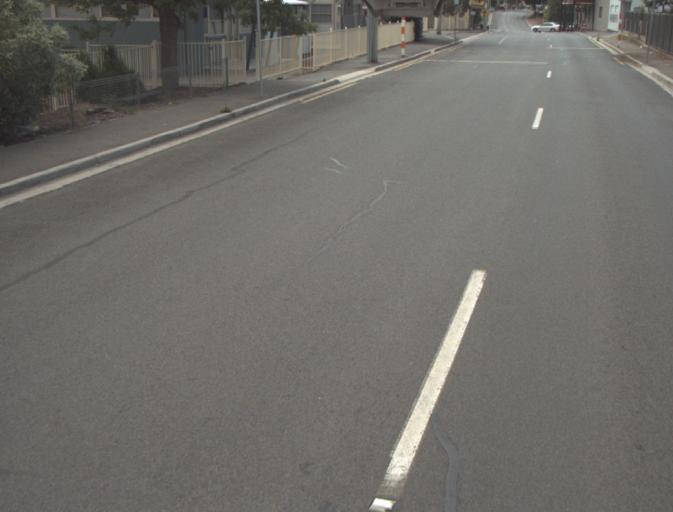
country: AU
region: Tasmania
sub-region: Launceston
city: Newstead
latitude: -41.4595
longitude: 147.2014
